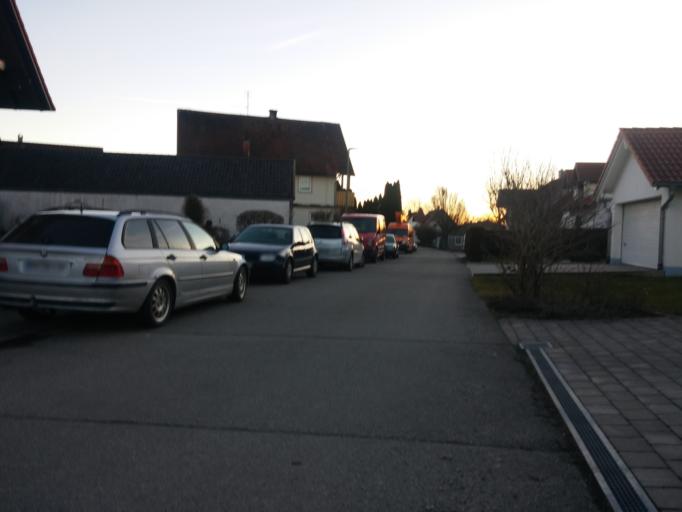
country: DE
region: Bavaria
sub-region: Swabia
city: Niederrieden
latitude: 48.0593
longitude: 10.1906
